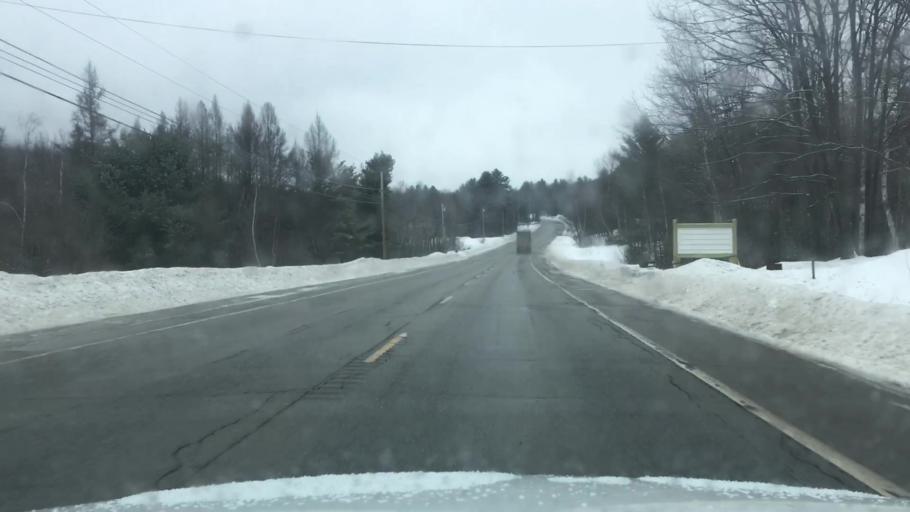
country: US
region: Maine
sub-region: Oxford County
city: Peru
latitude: 44.5697
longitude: -70.3731
